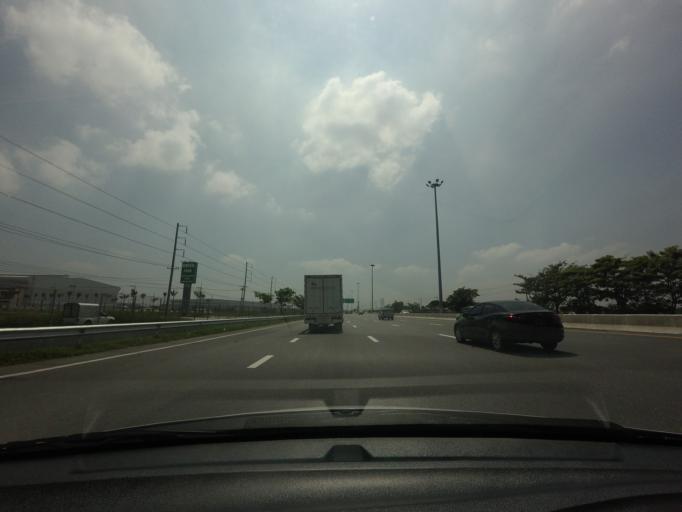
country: TH
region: Chachoengsao
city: Bang Pakong
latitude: 13.5676
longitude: 100.9852
